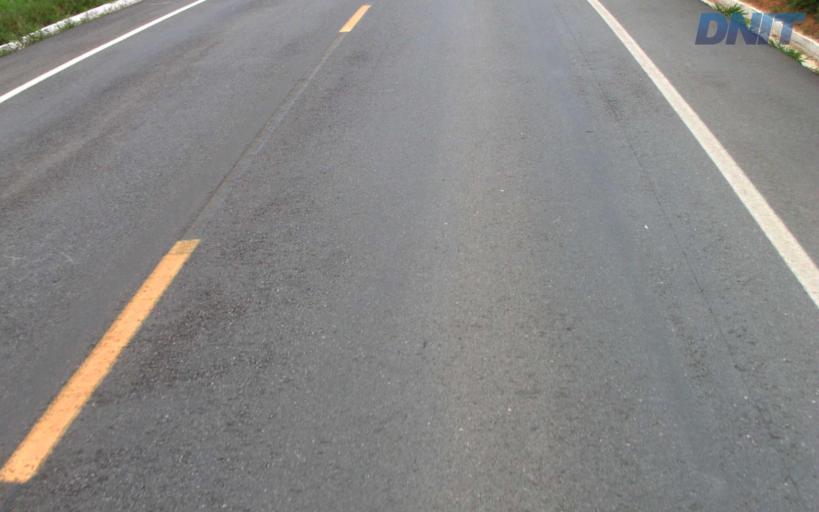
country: BR
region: Minas Gerais
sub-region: Governador Valadares
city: Governador Valadares
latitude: -18.9338
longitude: -42.0495
